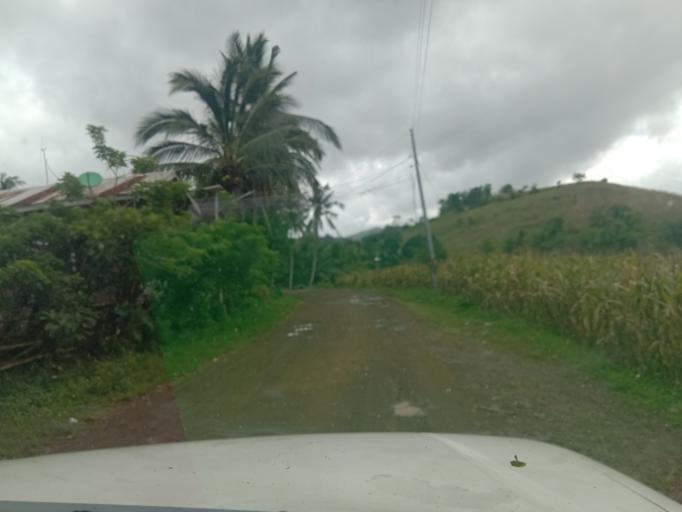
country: PH
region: Western Visayas
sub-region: Province of Capiz
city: Lantangan
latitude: 11.3728
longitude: 122.8926
